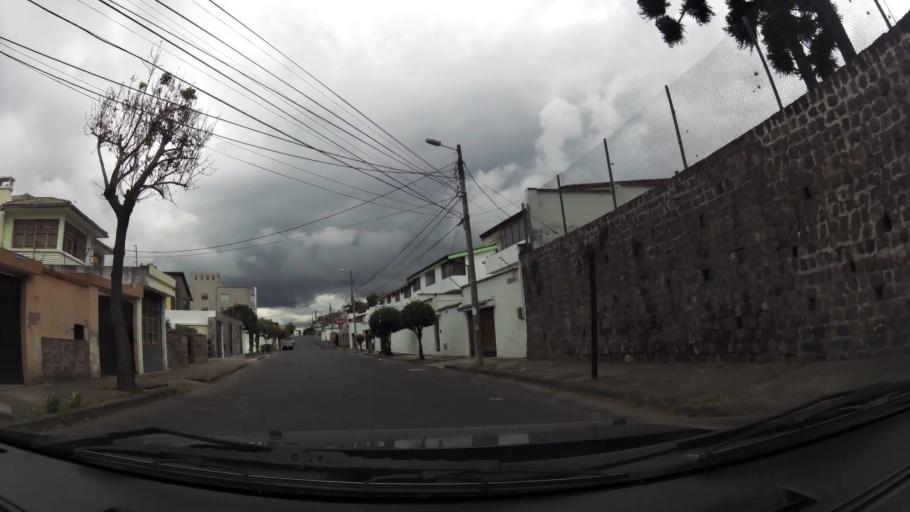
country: EC
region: Pichincha
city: Quito
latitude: -0.1499
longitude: -78.4939
